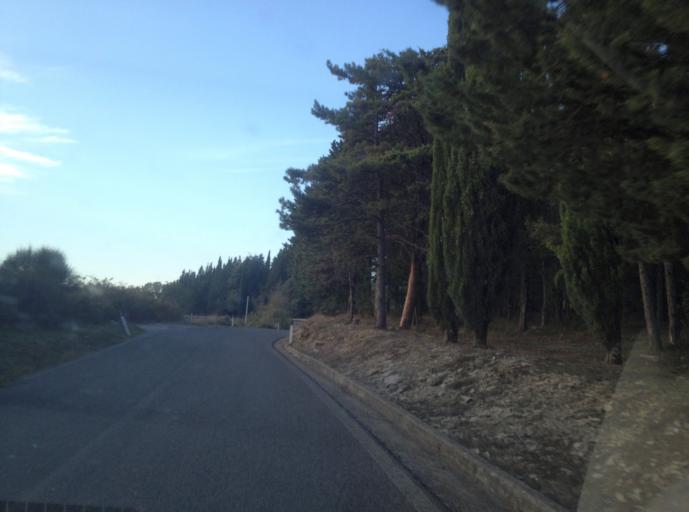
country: IT
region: Tuscany
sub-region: Provincia di Siena
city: Castellina in Chianti
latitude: 43.4469
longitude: 11.2985
